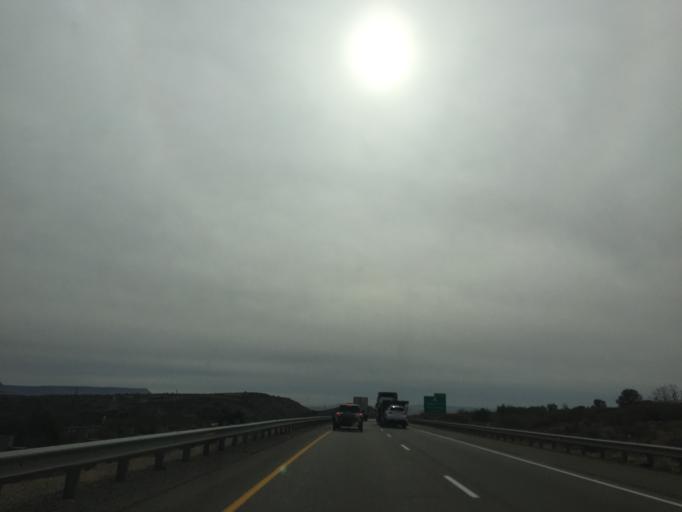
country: US
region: Utah
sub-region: Washington County
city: Toquerville
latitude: 37.2954
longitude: -113.3000
